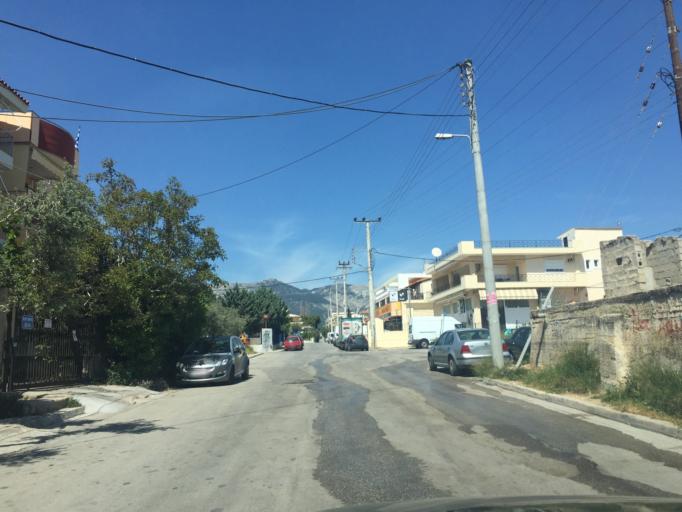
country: GR
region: Attica
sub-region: Nomarchia Anatolikis Attikis
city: Acharnes
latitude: 38.0940
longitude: 23.7314
